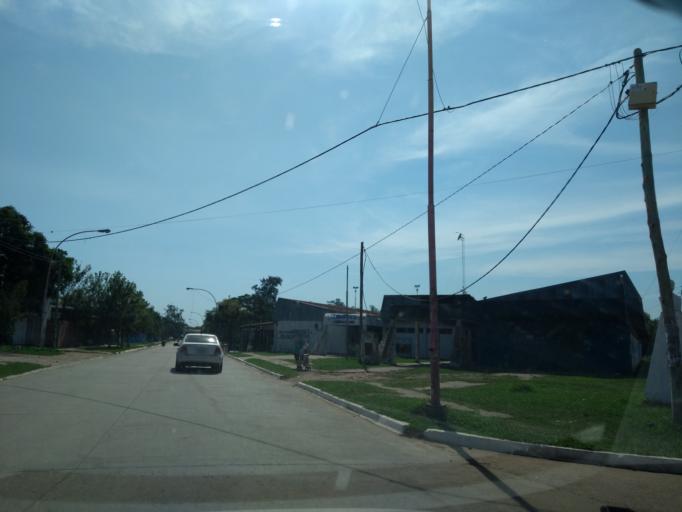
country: AR
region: Chaco
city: Barranqueras
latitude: -27.4639
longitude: -58.9488
